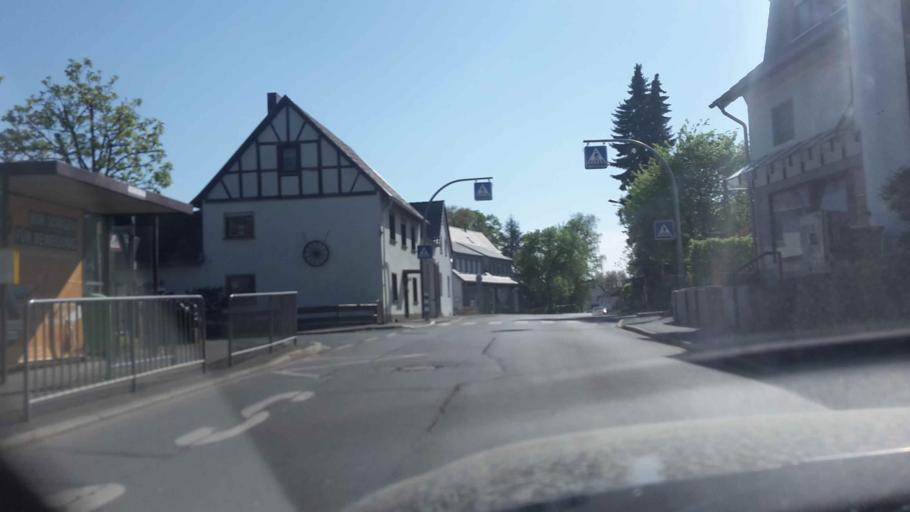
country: DE
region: Rheinland-Pfalz
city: Windhagen
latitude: 50.6871
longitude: 7.3368
